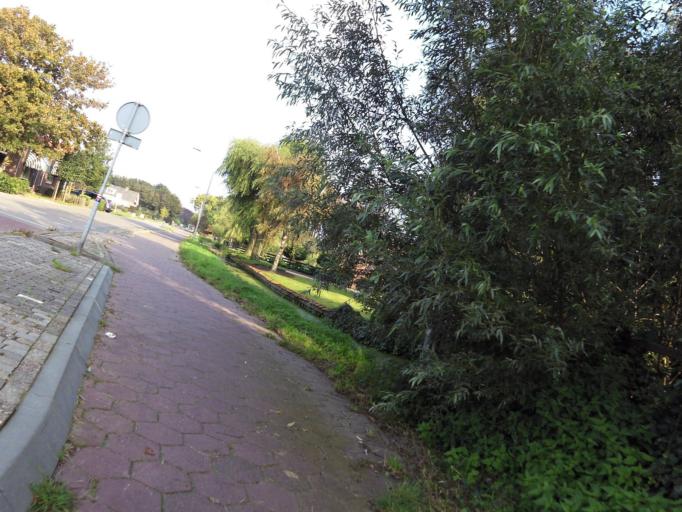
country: NL
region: South Holland
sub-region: Gemeente Rijnwoude
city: Benthuizen
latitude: 52.0950
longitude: 4.5574
